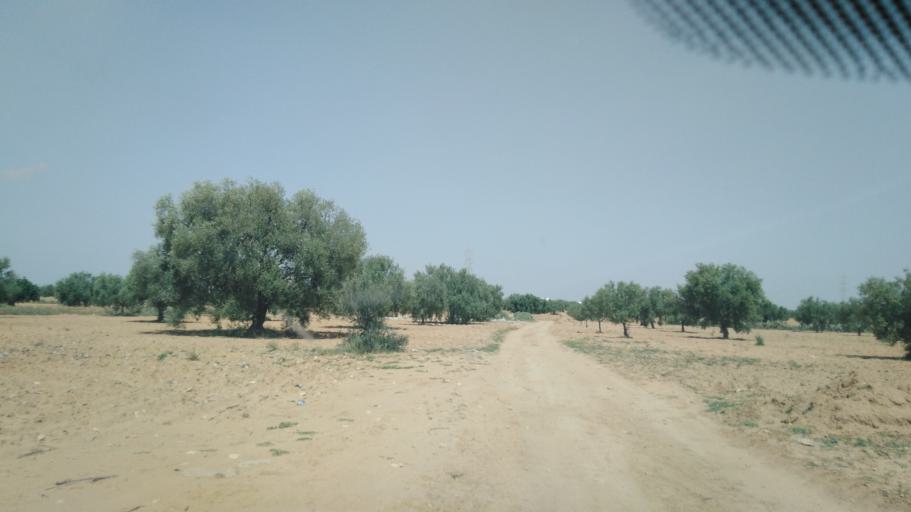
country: TN
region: Safaqis
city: Sfax
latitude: 34.7373
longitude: 10.5733
